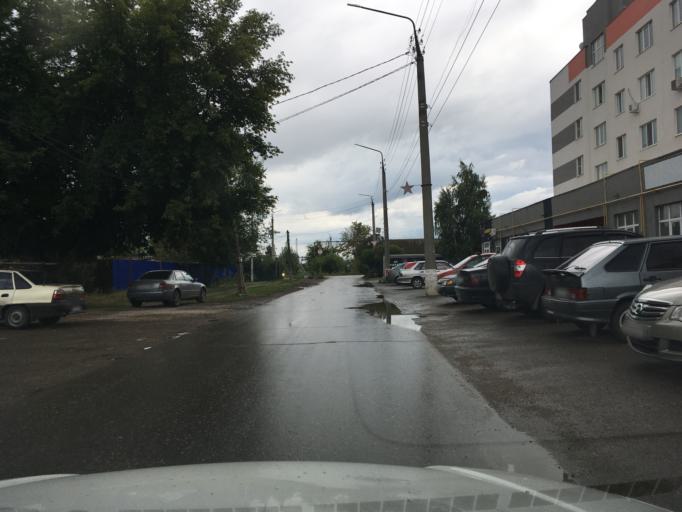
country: RU
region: Samara
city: Bezenchuk
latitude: 52.9807
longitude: 49.4388
